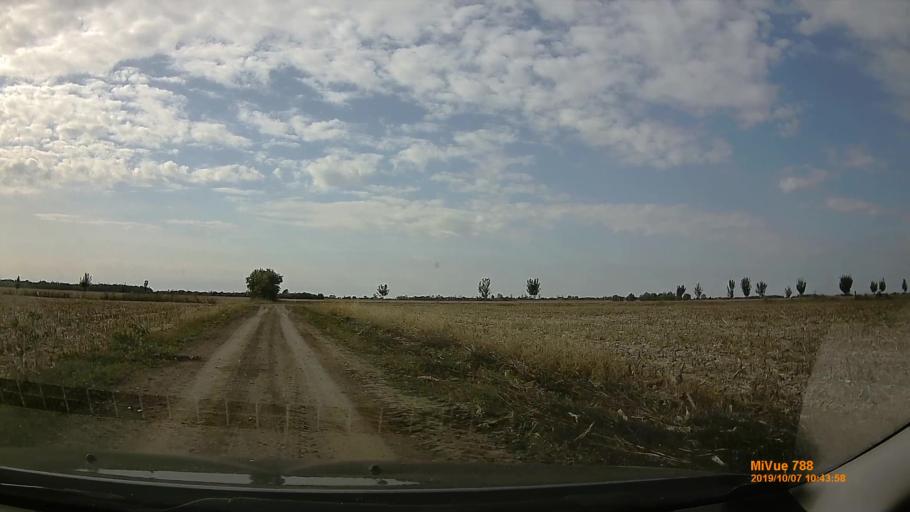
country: HU
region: Bekes
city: Kondoros
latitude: 46.7336
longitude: 20.8333
